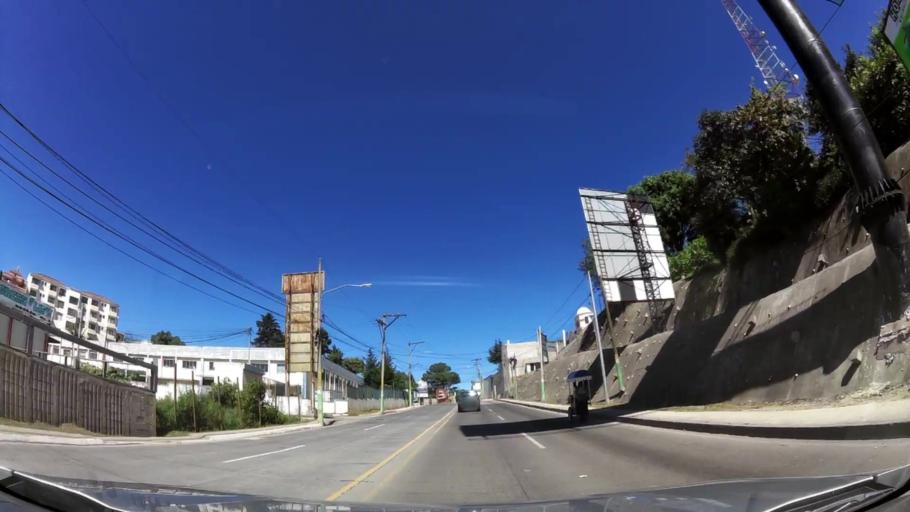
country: GT
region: Guatemala
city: San Jose Pinula
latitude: 14.5449
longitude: -90.4228
